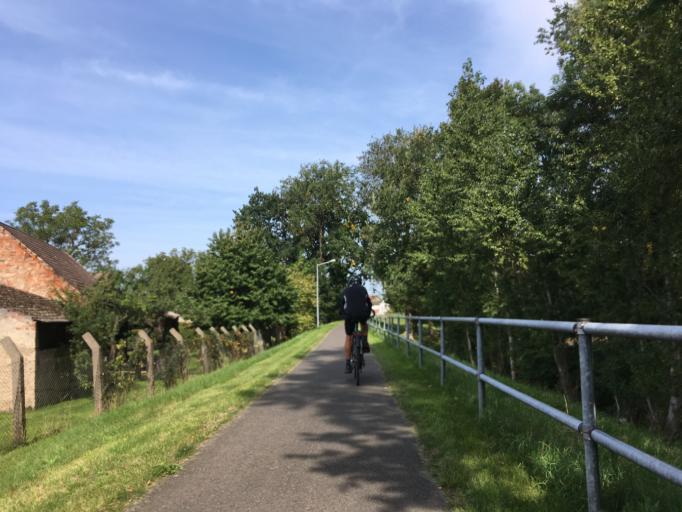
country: DE
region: Brandenburg
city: Guben
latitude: 51.9743
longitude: 14.7014
